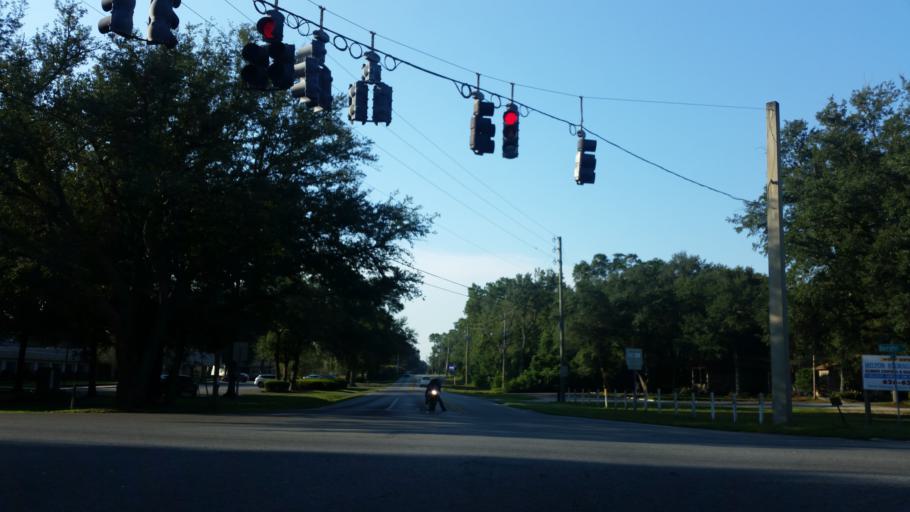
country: US
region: Florida
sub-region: Santa Rosa County
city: Milton
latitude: 30.6312
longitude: -87.0642
